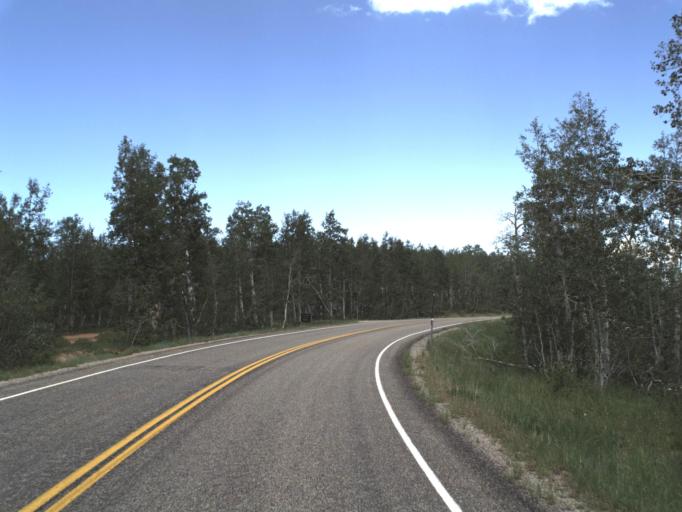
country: US
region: Utah
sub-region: Weber County
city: Wolf Creek
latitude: 41.4442
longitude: -111.5056
